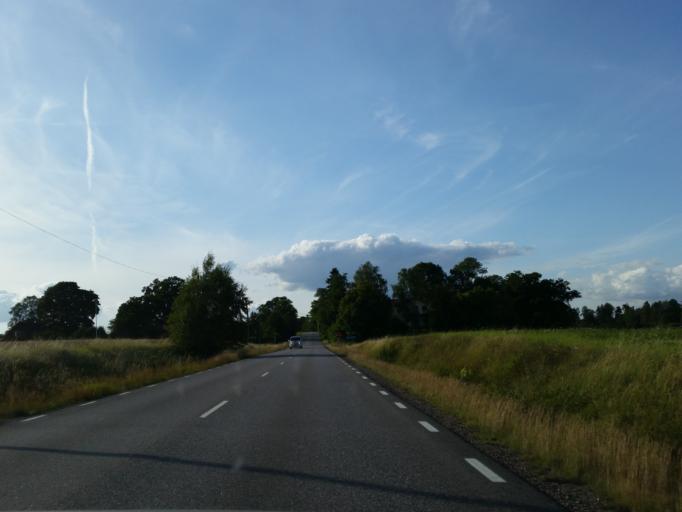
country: SE
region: Stockholm
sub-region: Sodertalje Kommun
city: Molnbo
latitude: 58.9967
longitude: 17.4092
